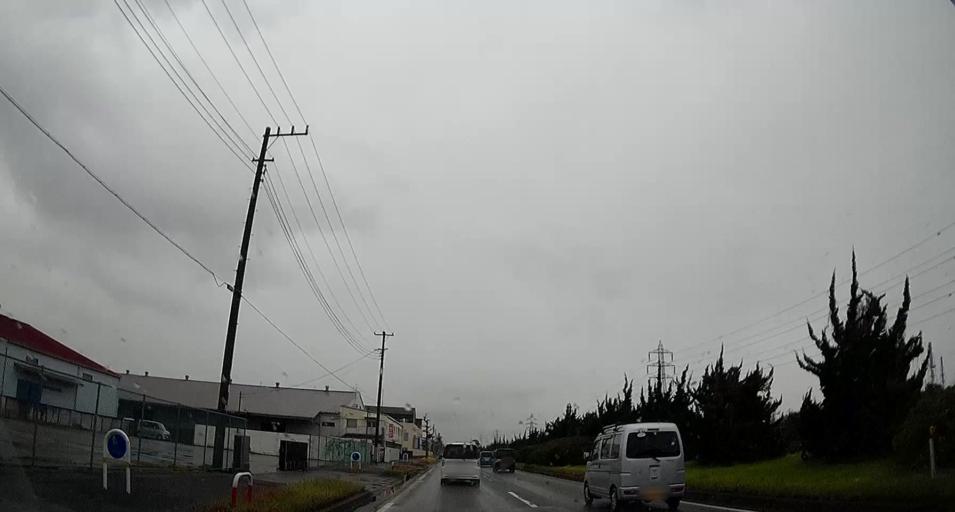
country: JP
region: Chiba
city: Ichihara
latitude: 35.5182
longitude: 140.0608
